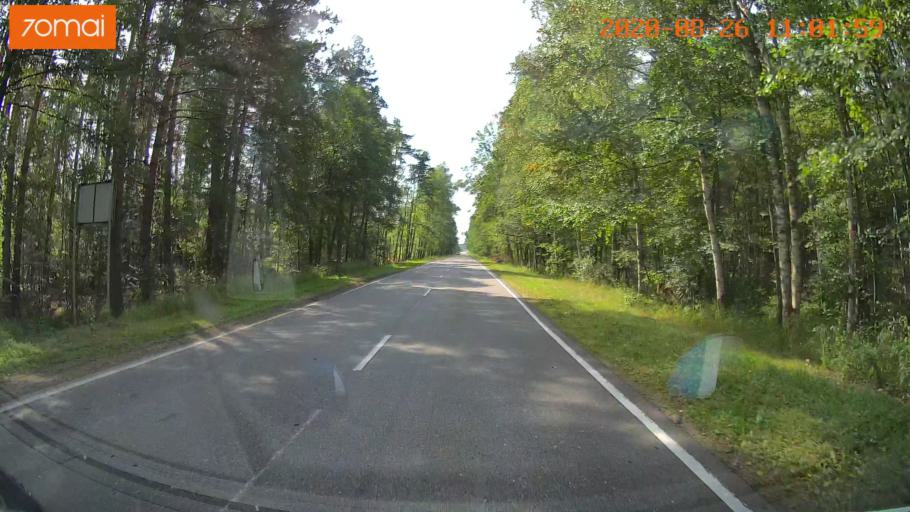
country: RU
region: Rjazan
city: Izhevskoye
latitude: 54.5567
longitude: 41.2267
